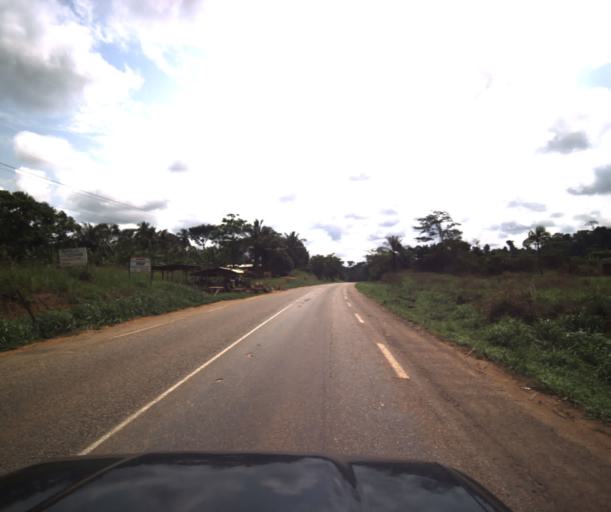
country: CM
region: Centre
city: Eseka
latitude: 3.8687
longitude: 10.6067
